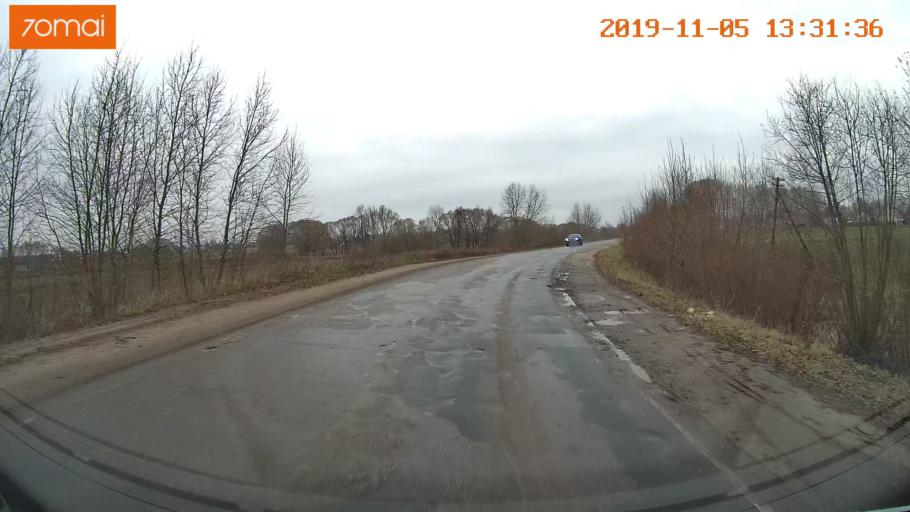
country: RU
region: Ivanovo
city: Shuya
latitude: 56.8776
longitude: 41.3937
